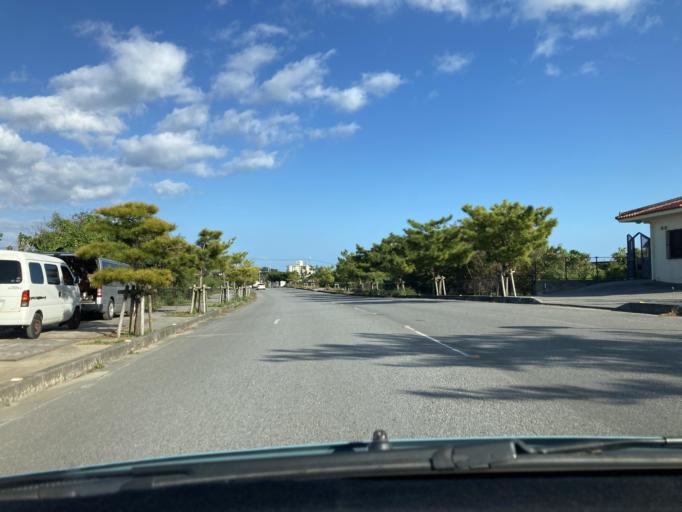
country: JP
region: Okinawa
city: Gushikawa
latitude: 26.3839
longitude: 127.8494
